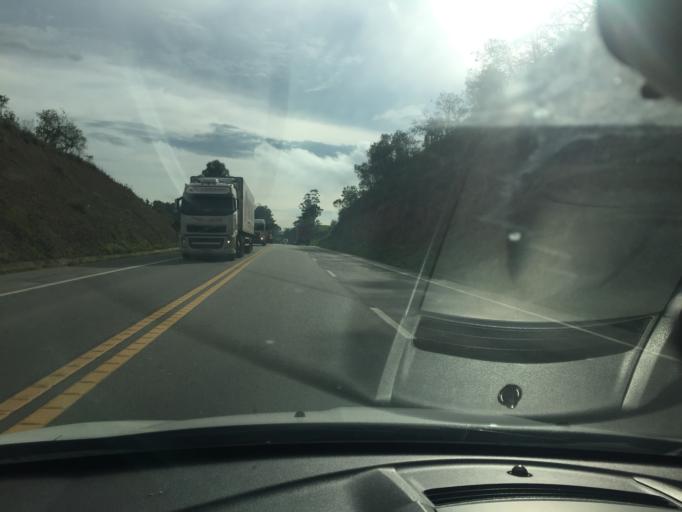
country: BR
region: Sao Paulo
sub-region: Campo Limpo Paulista
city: Campo Limpo Paulista
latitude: -23.1719
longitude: -46.7708
